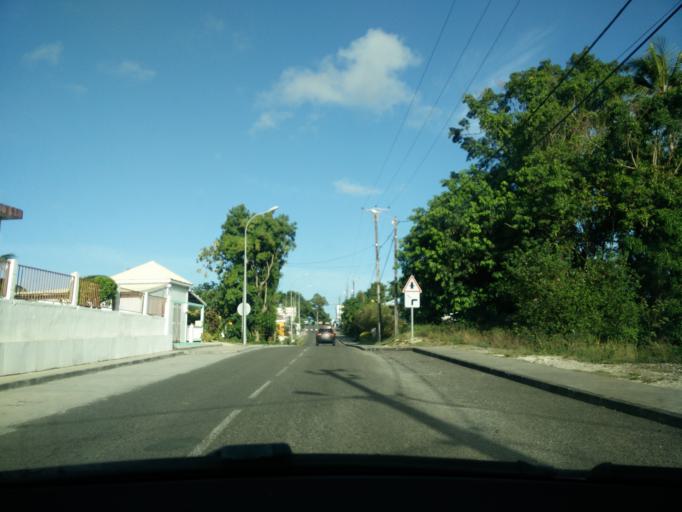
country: GP
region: Guadeloupe
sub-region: Guadeloupe
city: Sainte-Anne
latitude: 16.2629
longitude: -61.4242
